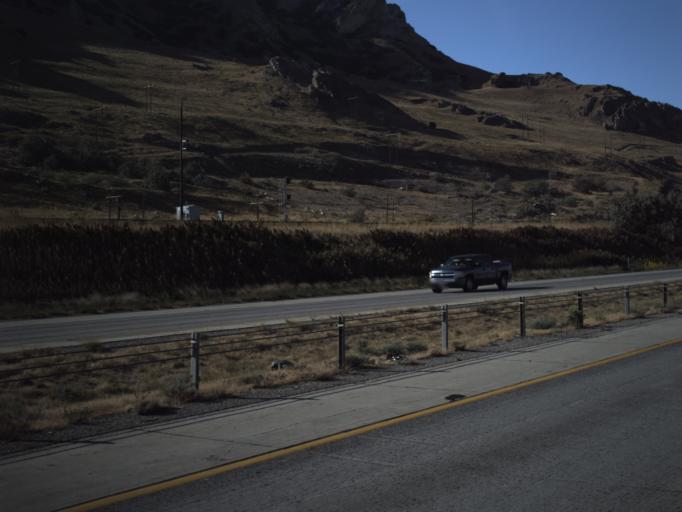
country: US
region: Utah
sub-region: Tooele County
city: Stansbury park
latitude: 40.7132
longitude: -112.2433
